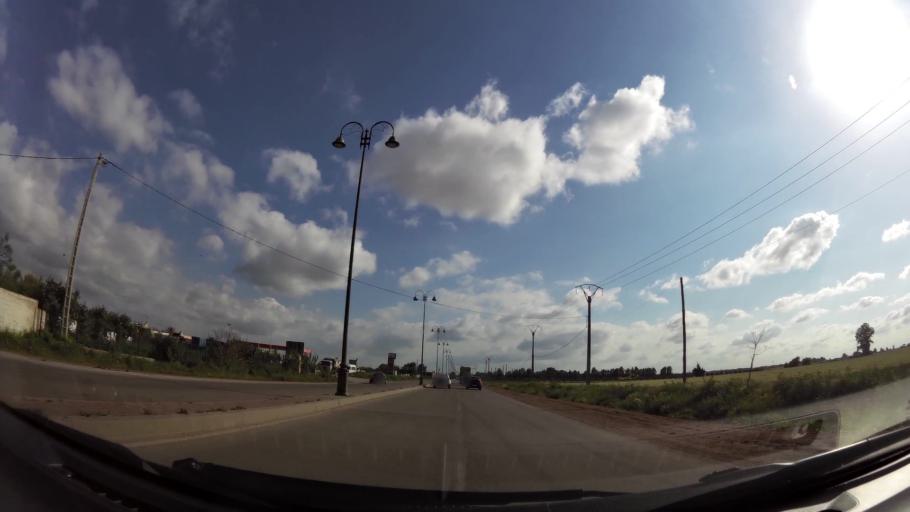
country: MA
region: Chaouia-Ouardigha
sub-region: Settat Province
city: Berrechid
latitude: 33.2908
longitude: -7.5761
